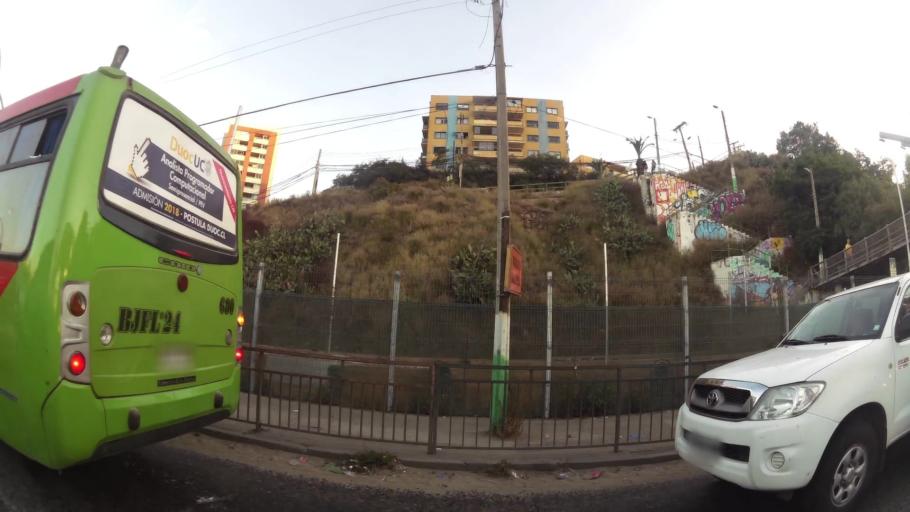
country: CL
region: Valparaiso
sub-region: Provincia de Valparaiso
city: Valparaiso
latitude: -33.0330
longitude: -71.5906
